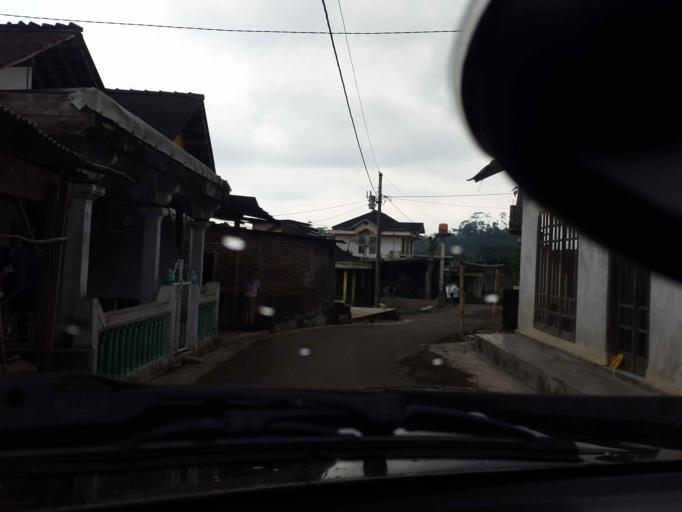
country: ID
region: Central Java
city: Wonosobo
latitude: -7.3607
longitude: 109.9608
